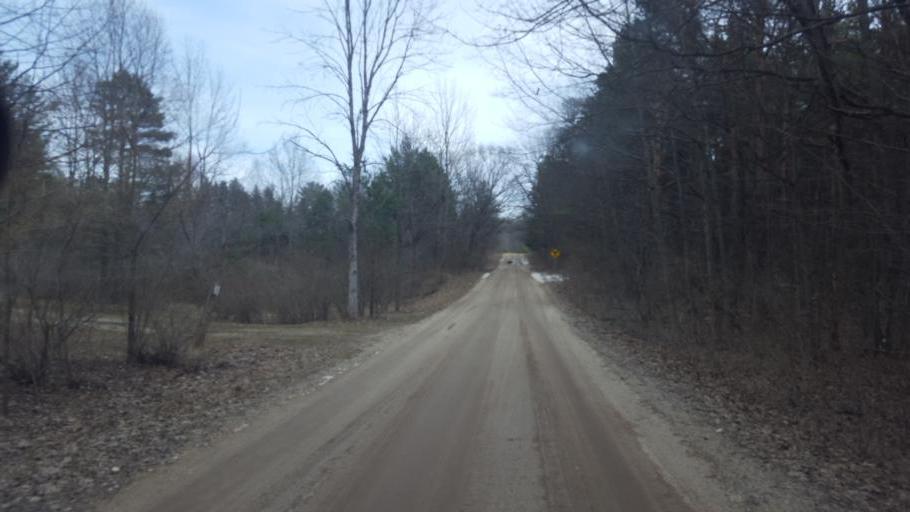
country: US
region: Michigan
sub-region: Isabella County
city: Lake Isabella
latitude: 43.6791
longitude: -85.1299
